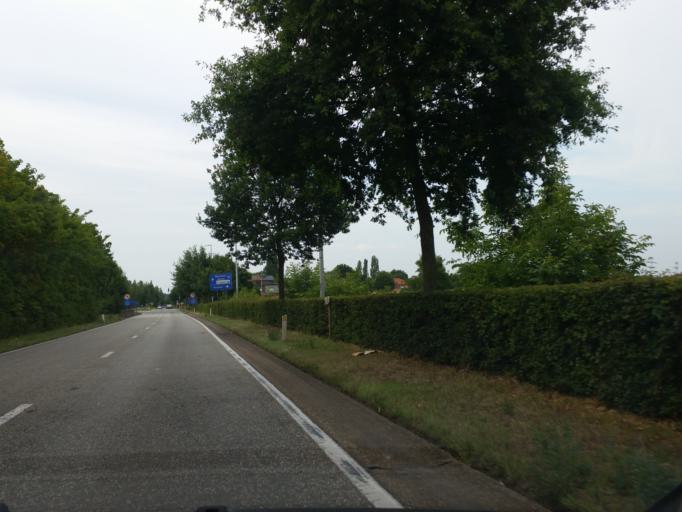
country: BE
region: Flanders
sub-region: Provincie Vlaams-Brabant
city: Vilvoorde
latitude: 50.9314
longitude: 4.4509
